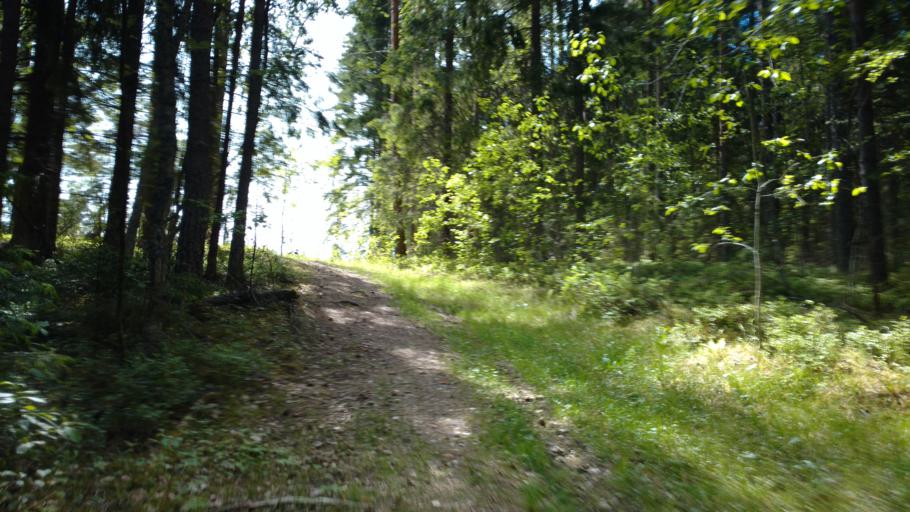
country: FI
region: Varsinais-Suomi
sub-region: Salo
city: Salo
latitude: 60.3705
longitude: 23.1840
